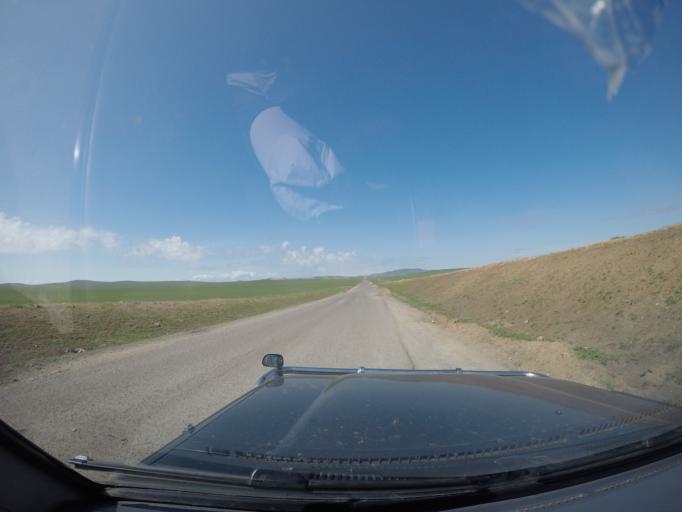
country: MN
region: Suhbaatar
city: Bayasgalant
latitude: 47.3439
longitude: 111.5755
